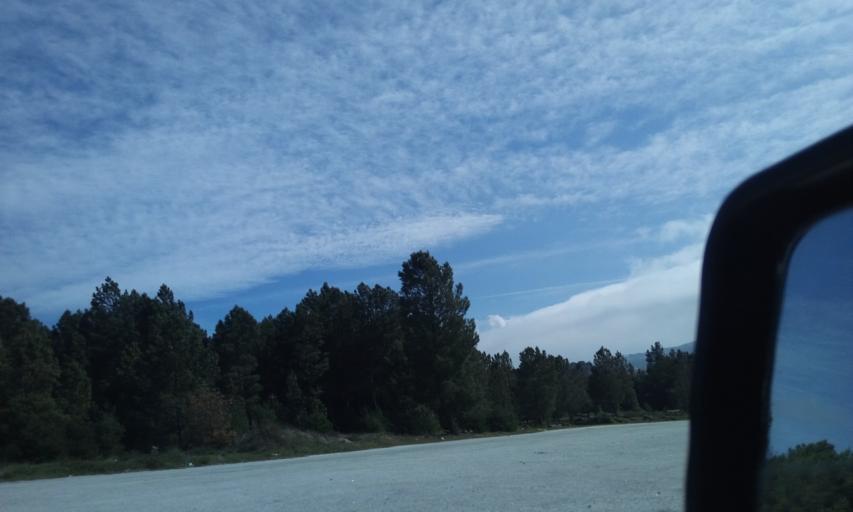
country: PT
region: Guarda
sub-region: Celorico da Beira
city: Celorico da Beira
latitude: 40.6339
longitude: -7.4043
